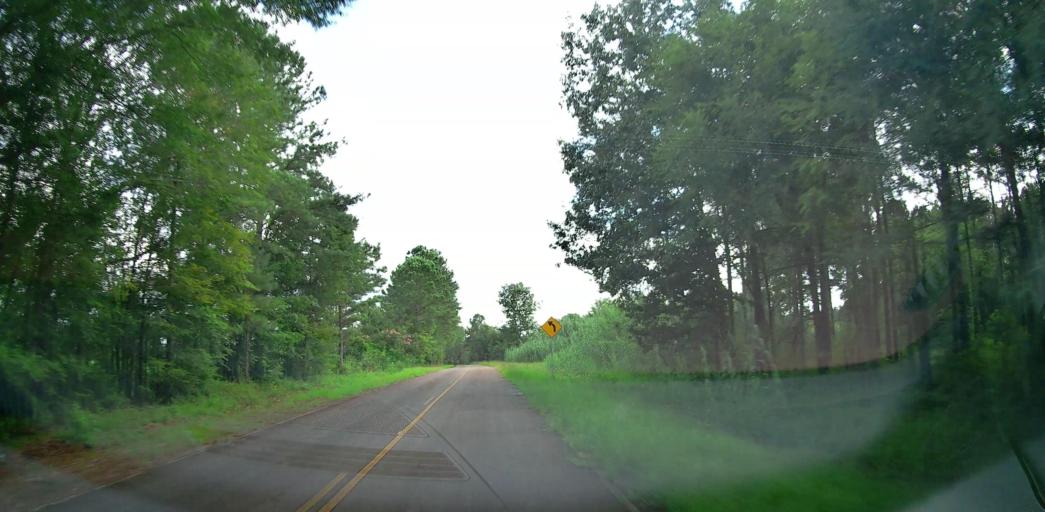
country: US
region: Georgia
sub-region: Bleckley County
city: Cochran
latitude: 32.4396
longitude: -83.4525
